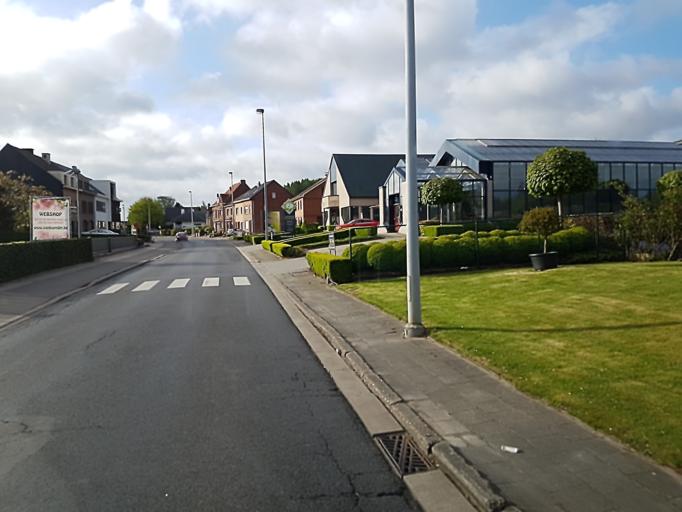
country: BE
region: Flanders
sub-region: Provincie Oost-Vlaanderen
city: Temse
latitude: 51.1311
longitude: 4.1936
